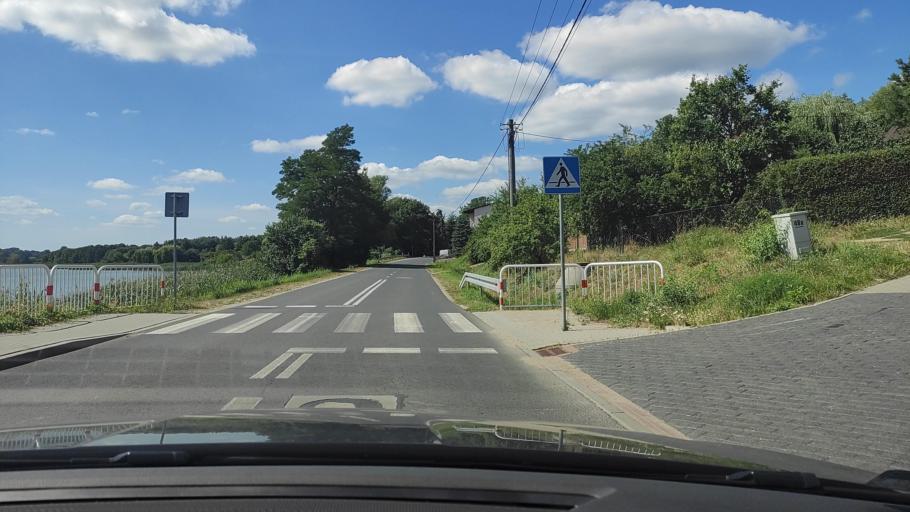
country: PL
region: Greater Poland Voivodeship
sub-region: Powiat poznanski
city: Kostrzyn
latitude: 52.4777
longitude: 17.1808
